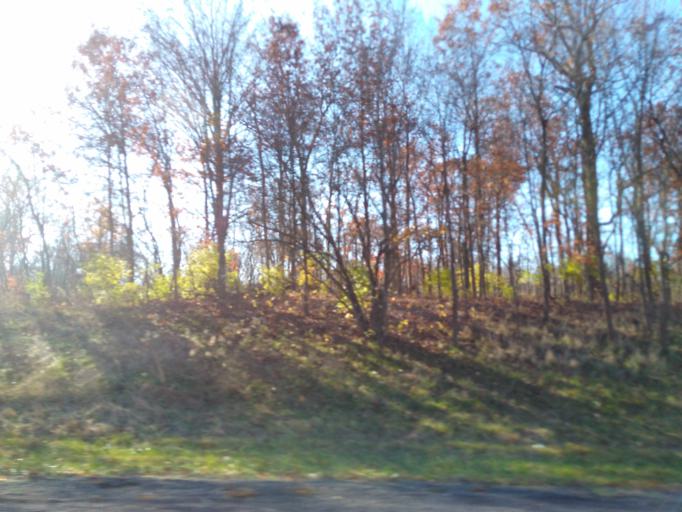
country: US
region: Illinois
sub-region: Madison County
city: Highland
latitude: 38.7864
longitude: -89.6655
